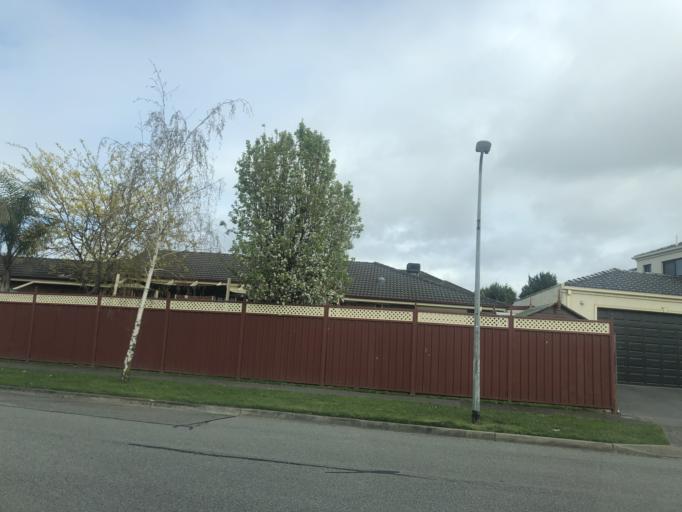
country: AU
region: Victoria
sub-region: Knox
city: Rowville
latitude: -37.9350
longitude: 145.2445
